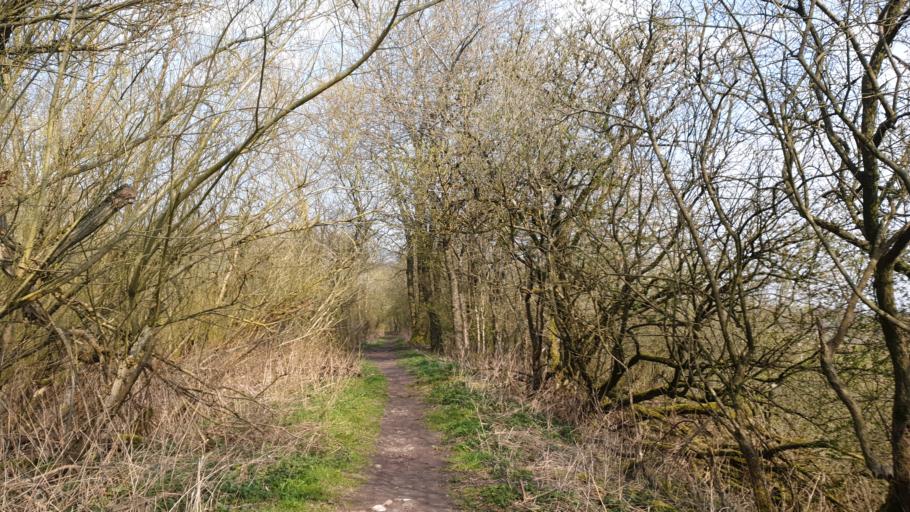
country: DK
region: Central Jutland
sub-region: Hedensted Kommune
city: Hedensted
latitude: 55.8100
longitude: 9.7034
